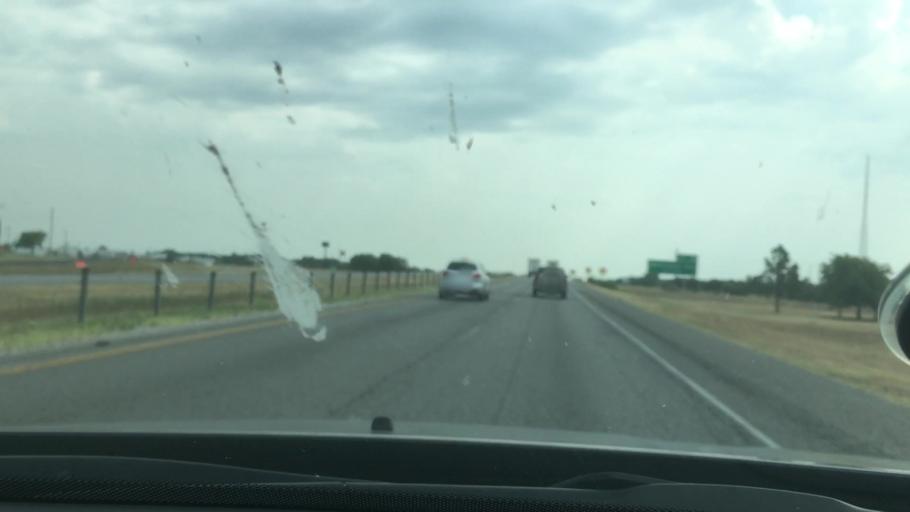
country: US
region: Oklahoma
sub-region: Bryan County
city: Durant
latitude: 34.0174
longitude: -96.3914
